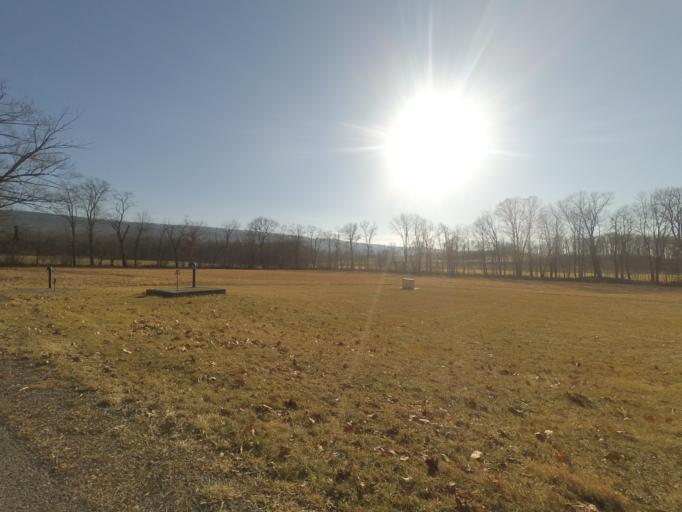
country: US
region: Pennsylvania
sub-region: Centre County
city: Boalsburg
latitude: 40.7698
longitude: -77.8276
